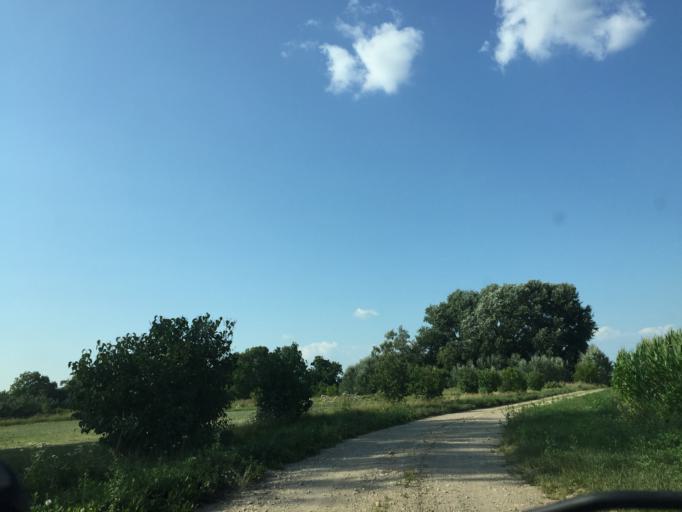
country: LV
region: Jelgava
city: Jelgava
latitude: 56.4678
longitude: 23.6749
